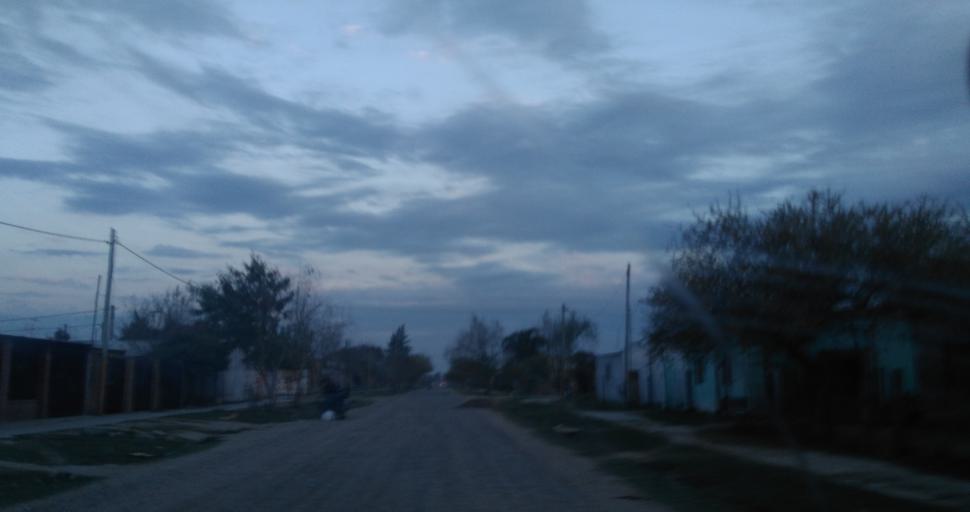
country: AR
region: Chaco
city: Resistencia
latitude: -27.4804
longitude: -59.0077
